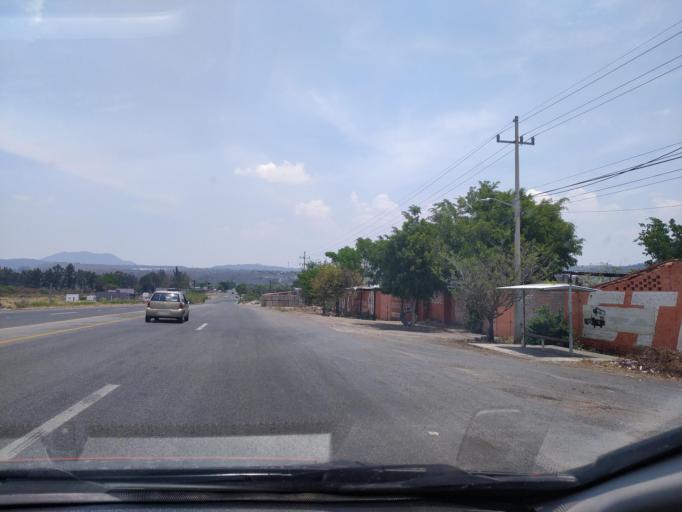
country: MX
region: Jalisco
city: Bellavista
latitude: 20.4088
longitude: -103.5939
